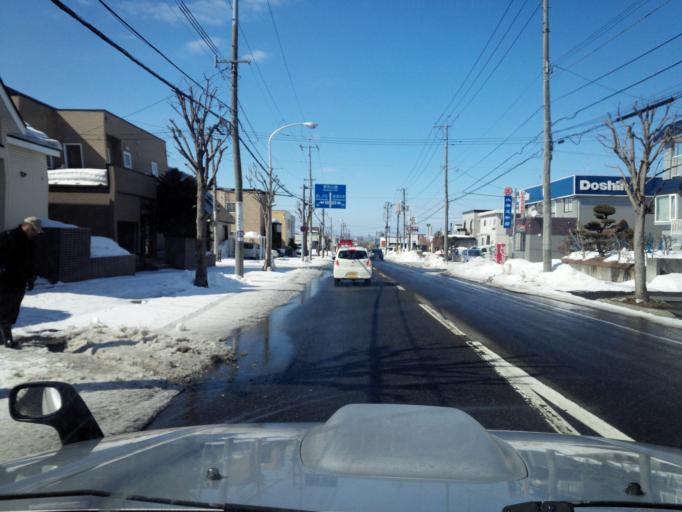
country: JP
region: Hokkaido
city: Kitahiroshima
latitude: 43.0112
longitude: 141.4712
